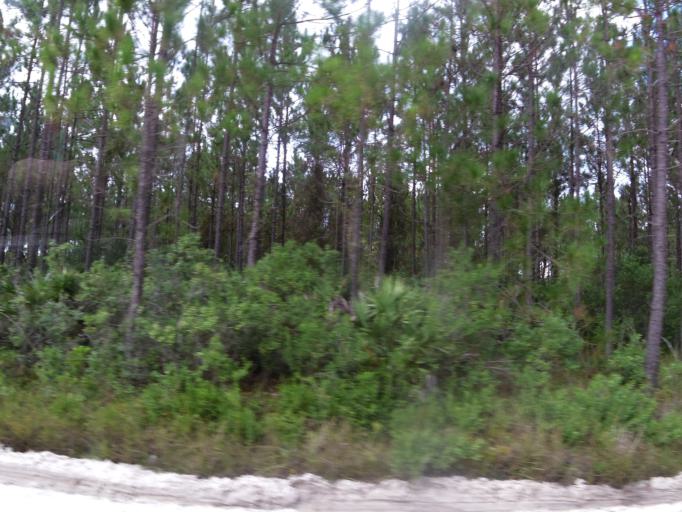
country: US
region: Florida
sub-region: Nassau County
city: Hilliard
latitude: 30.5935
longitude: -82.0496
